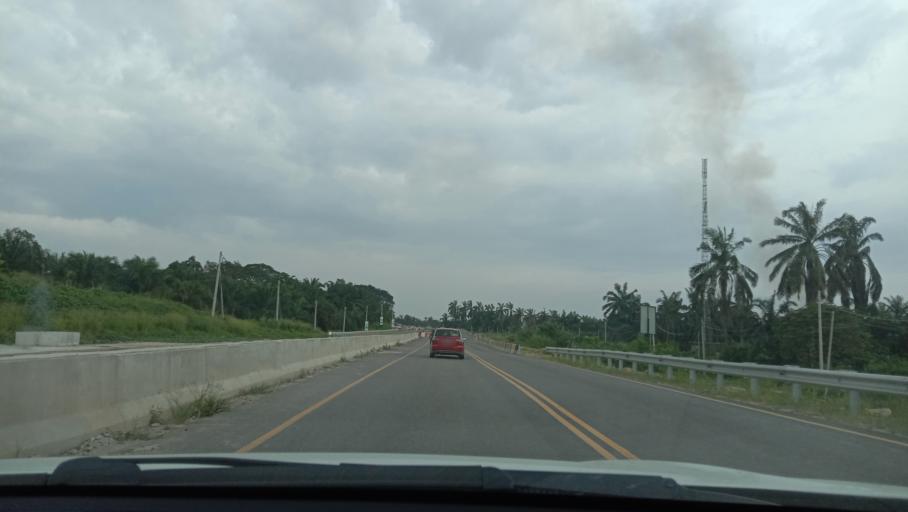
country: MY
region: Selangor
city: Batu Arang
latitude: 3.2681
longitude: 101.4551
